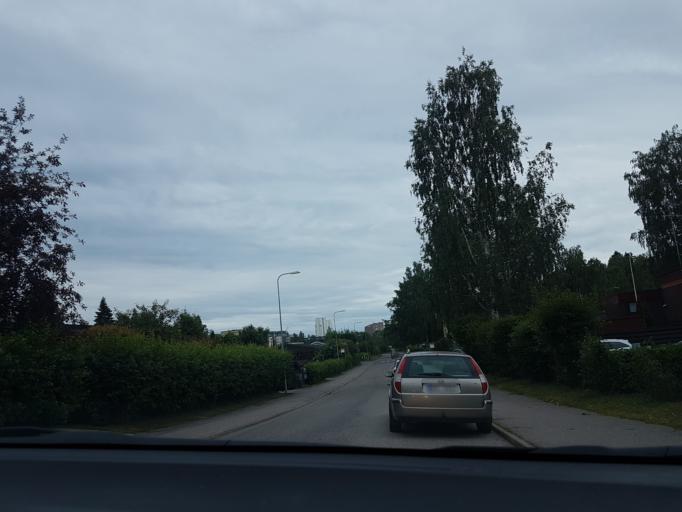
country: FI
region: Uusimaa
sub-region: Helsinki
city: Vantaa
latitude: 60.2115
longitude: 25.1252
